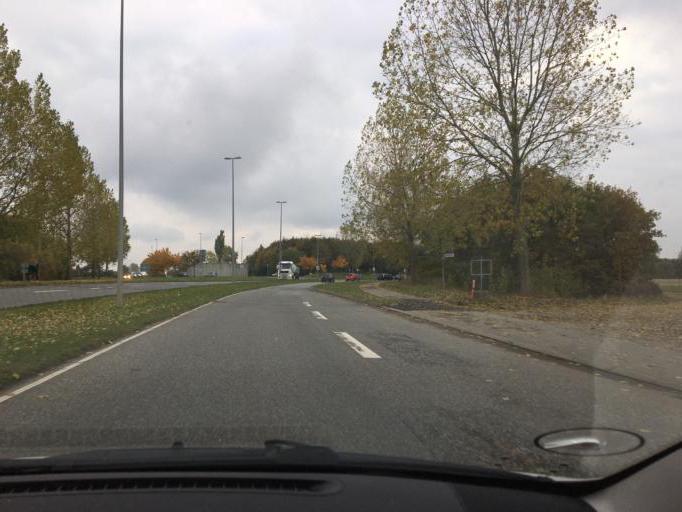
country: DK
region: South Denmark
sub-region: Fredericia Kommune
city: Fredericia
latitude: 55.5895
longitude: 9.7542
